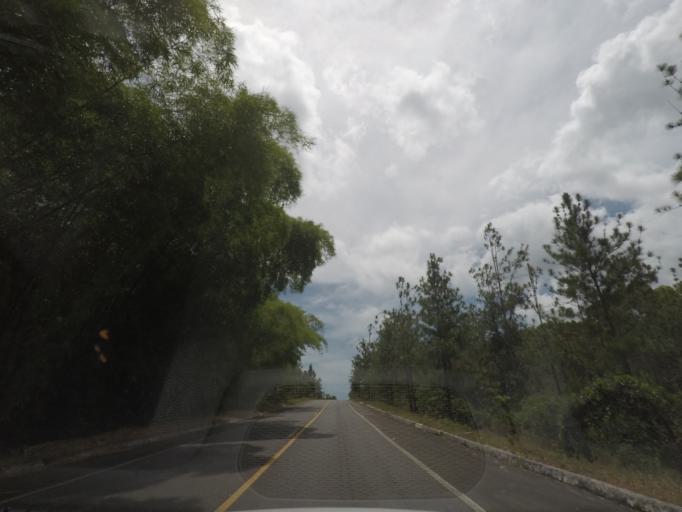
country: BR
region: Bahia
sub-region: Entre Rios
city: Entre Rios
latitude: -12.1187
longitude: -37.7879
